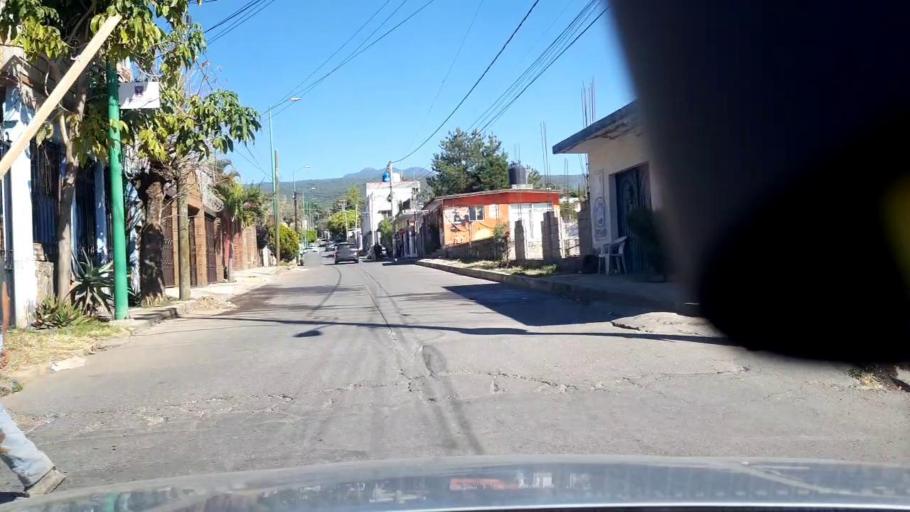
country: MX
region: Morelos
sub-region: Cuernavaca
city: Colonia los Cerritos
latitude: 18.9640
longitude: -99.2227
